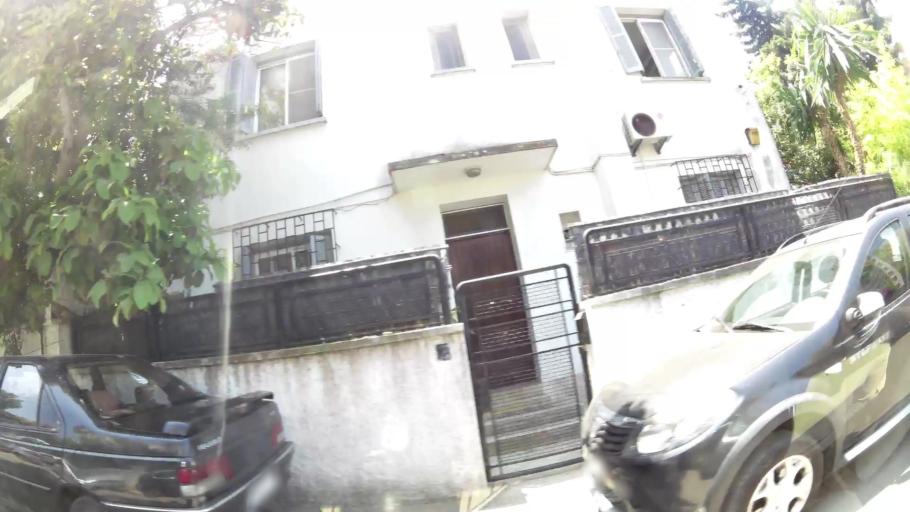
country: MA
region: Rabat-Sale-Zemmour-Zaer
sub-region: Rabat
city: Rabat
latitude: 34.0149
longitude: -6.8245
